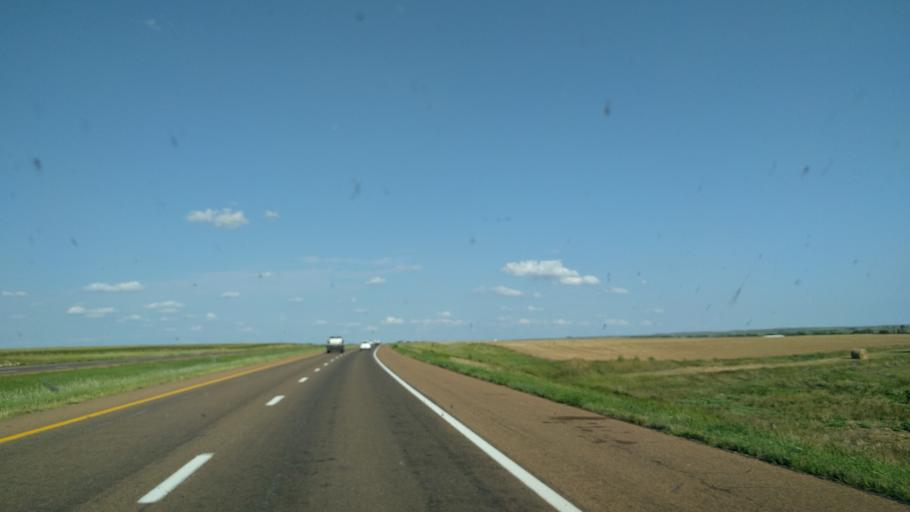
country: US
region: Kansas
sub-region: Ellis County
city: Ellis
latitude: 38.9487
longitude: -99.5218
